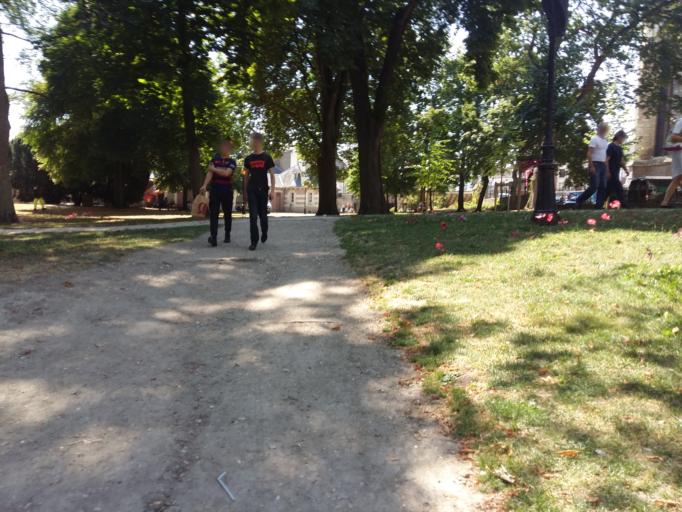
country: FR
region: Picardie
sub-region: Departement de la Somme
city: Amiens
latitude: 49.8950
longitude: 2.3034
